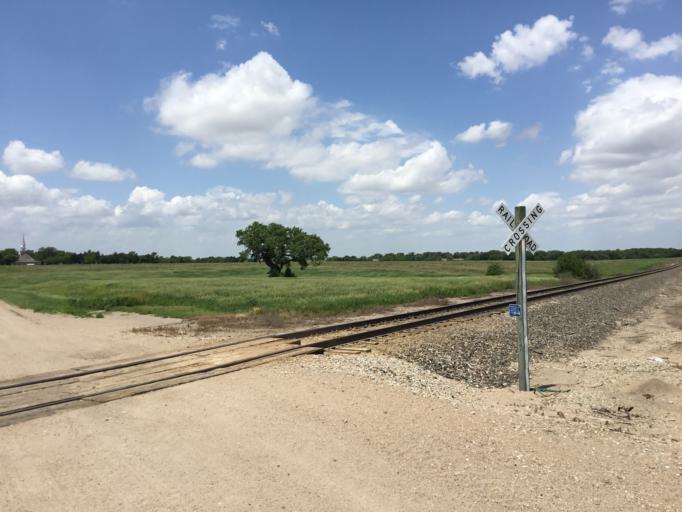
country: US
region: Kansas
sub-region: Cloud County
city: Concordia
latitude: 39.7117
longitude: -97.8603
